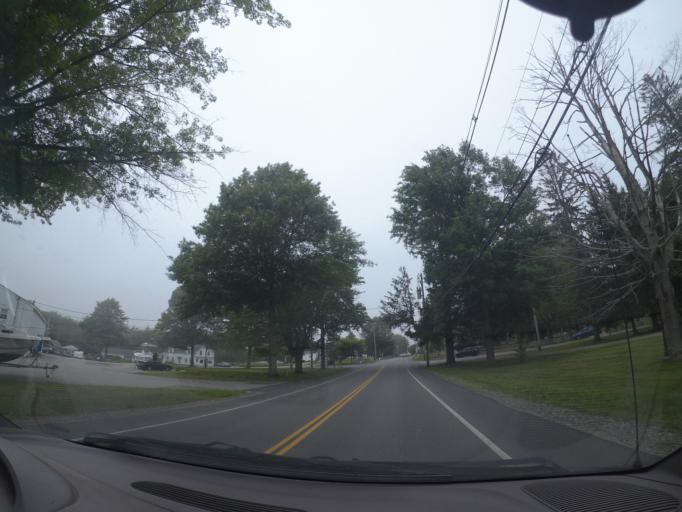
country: US
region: Maine
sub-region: York County
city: Arundel
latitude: 43.3804
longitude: -70.4770
